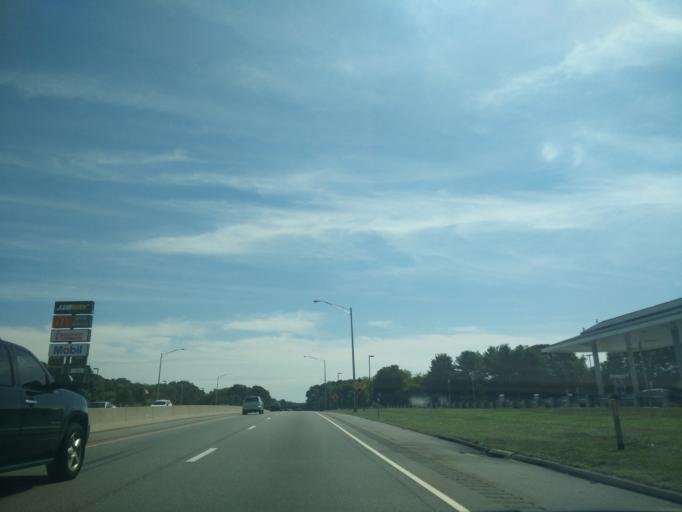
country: US
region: Connecticut
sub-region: New Haven County
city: Madison
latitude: 41.2910
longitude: -72.5808
